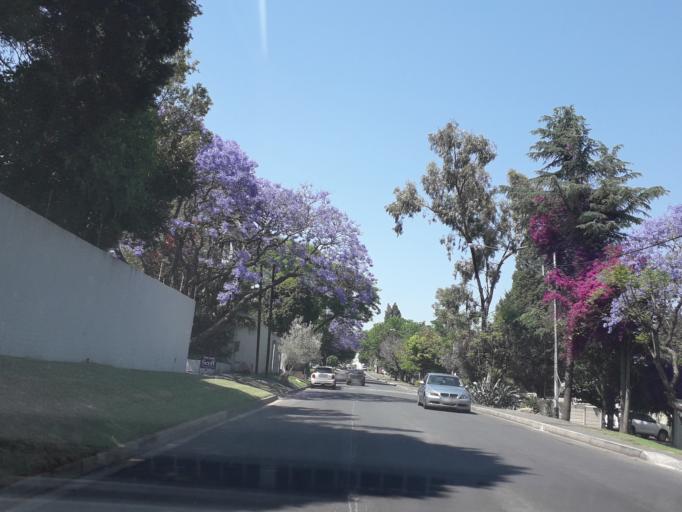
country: ZA
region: Gauteng
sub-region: City of Johannesburg Metropolitan Municipality
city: Johannesburg
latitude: -26.1208
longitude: 28.0207
